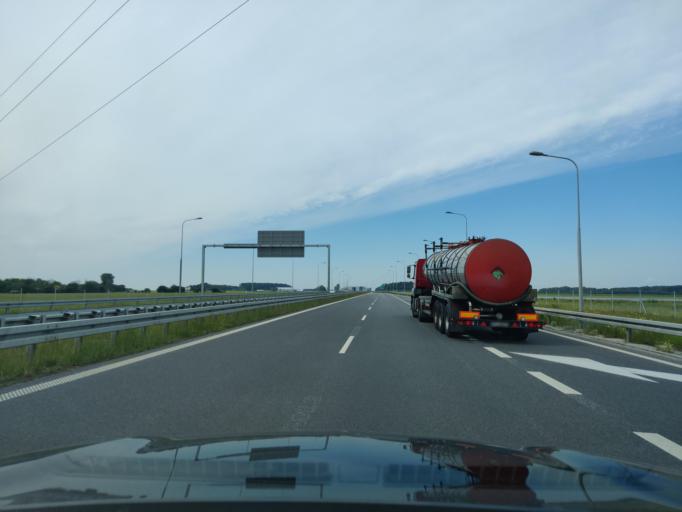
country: PL
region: Greater Poland Voivodeship
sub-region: Powiat poznanski
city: Steszew
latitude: 52.2655
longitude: 16.6632
